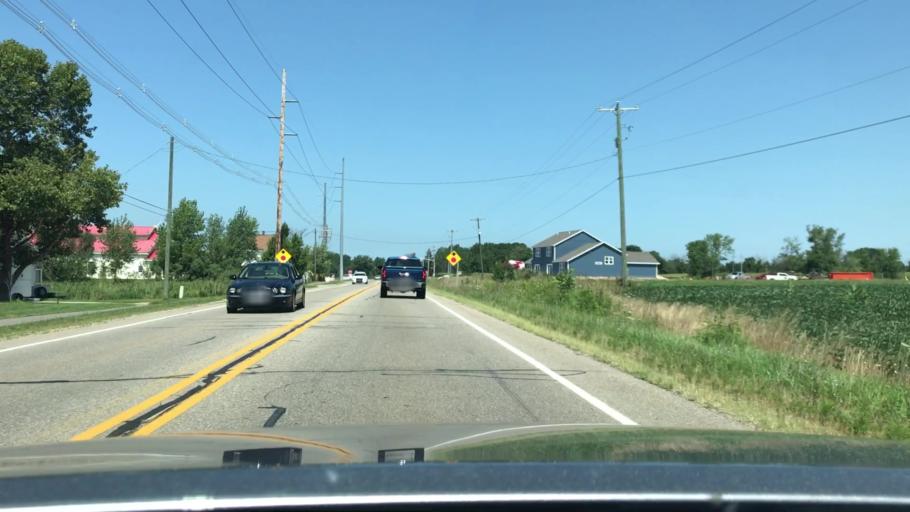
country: US
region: Michigan
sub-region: Ottawa County
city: Holland
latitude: 42.8391
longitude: -86.0789
